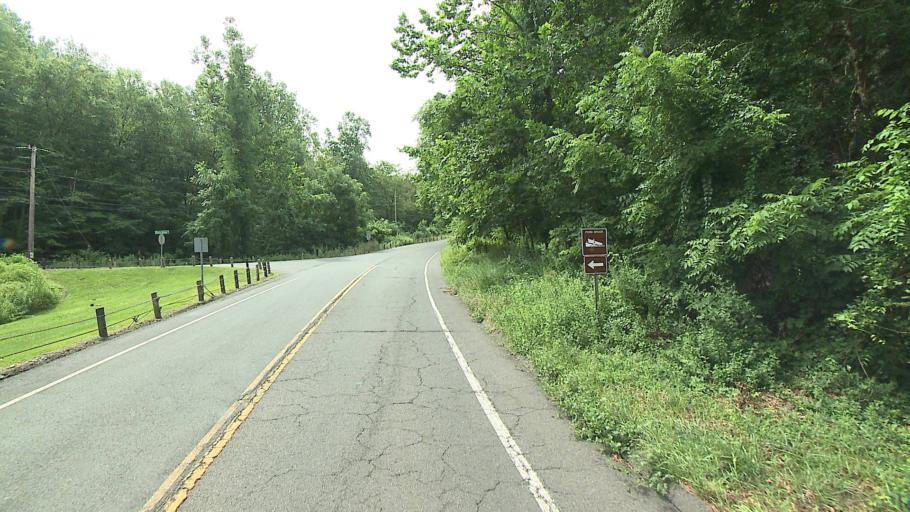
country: US
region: Connecticut
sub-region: Fairfield County
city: Newtown
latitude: 41.4754
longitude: -73.3512
